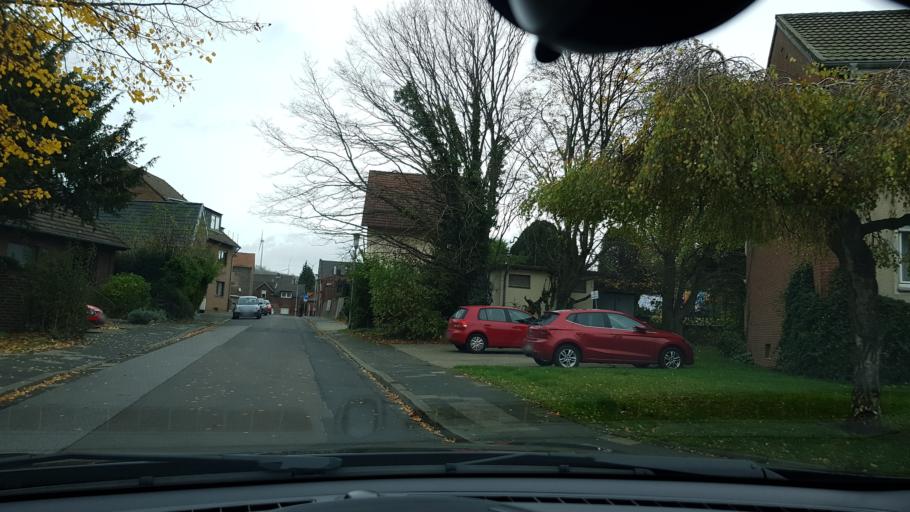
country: DE
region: North Rhine-Westphalia
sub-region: Regierungsbezirk Dusseldorf
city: Grevenbroich
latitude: 51.0432
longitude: 6.5776
